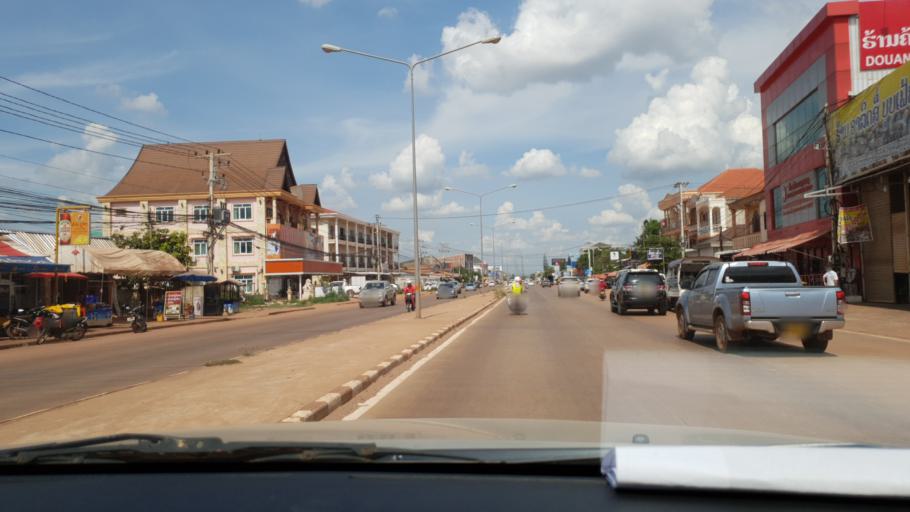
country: LA
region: Vientiane
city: Vientiane
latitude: 18.0322
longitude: 102.6441
